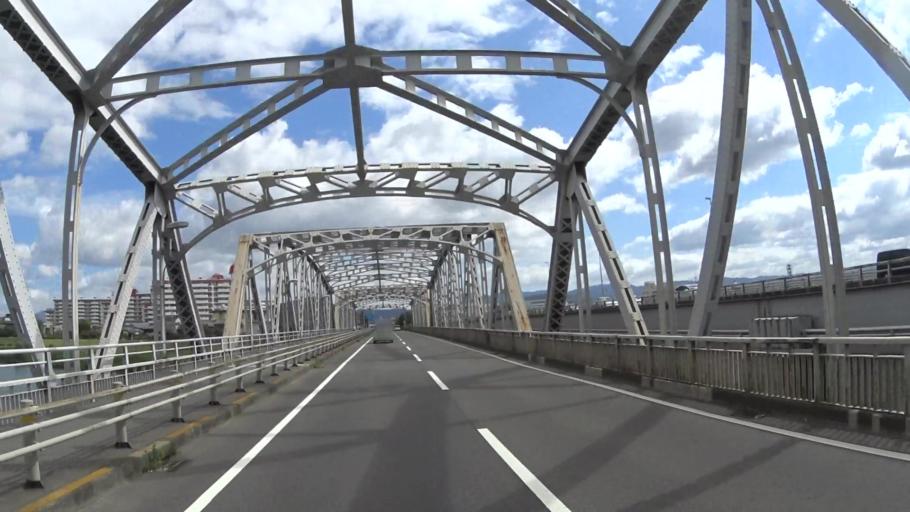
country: JP
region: Kyoto
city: Muko
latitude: 34.9647
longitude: 135.7214
